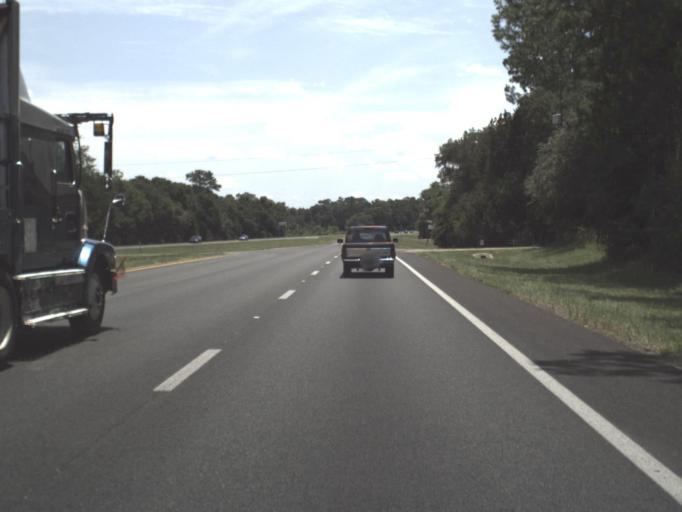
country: US
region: Florida
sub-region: Levy County
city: Manatee Road
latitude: 29.5940
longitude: -82.9673
